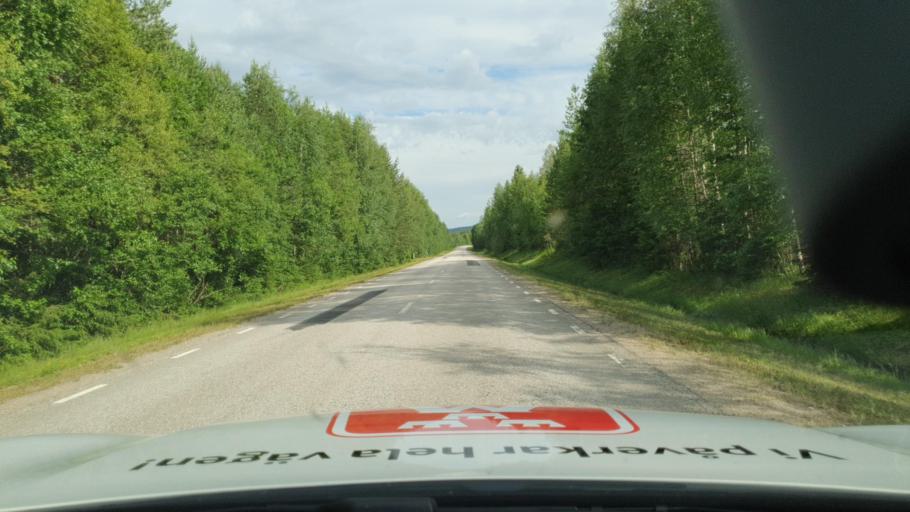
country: NO
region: Hedmark
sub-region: Trysil
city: Innbygda
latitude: 60.9197
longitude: 12.5354
